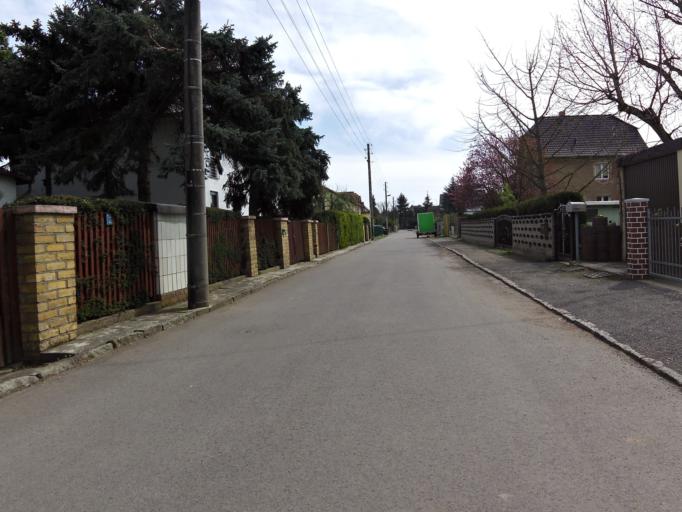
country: DE
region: Saxony
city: Markranstadt
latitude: 51.3149
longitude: 12.2742
